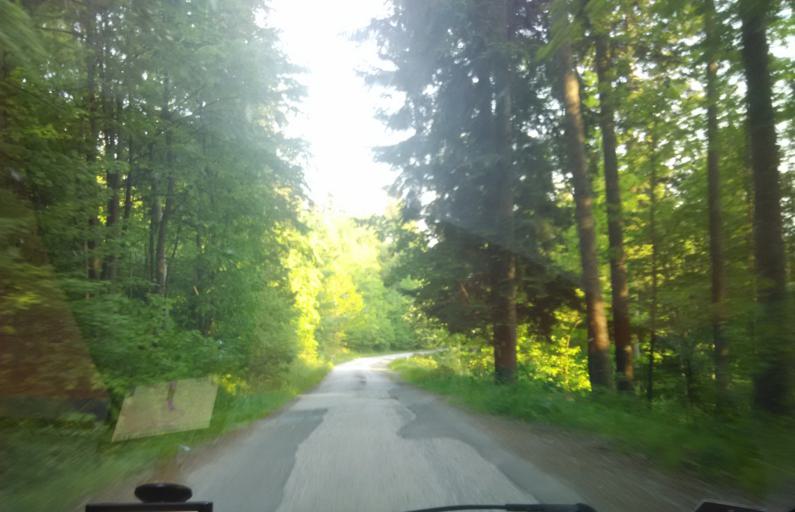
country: SK
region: Presovsky
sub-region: Okres Presov
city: Levoca
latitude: 49.0474
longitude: 20.6081
